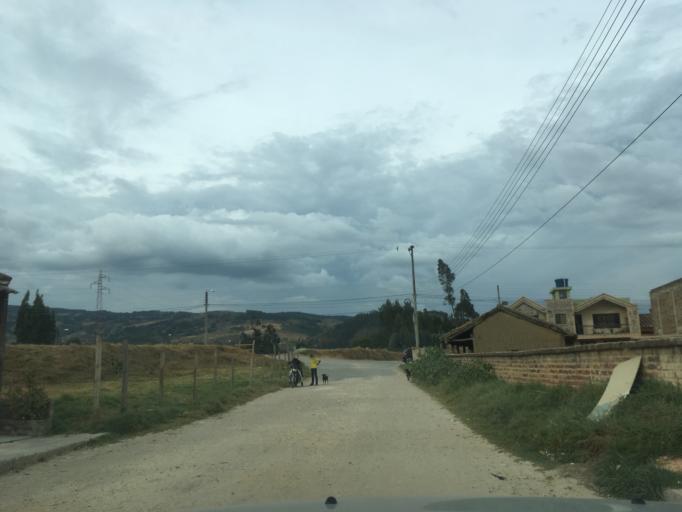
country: CO
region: Boyaca
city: Firavitoba
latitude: 5.6689
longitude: -72.9964
